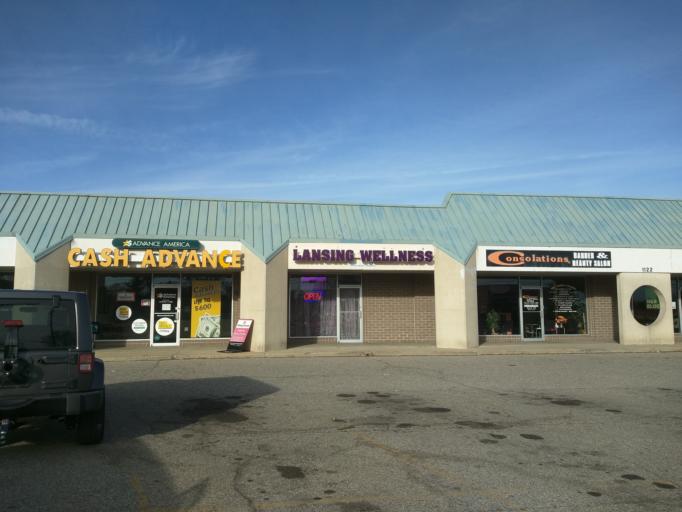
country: US
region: Michigan
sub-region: Ingham County
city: Lansing
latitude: 42.6979
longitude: -84.5689
